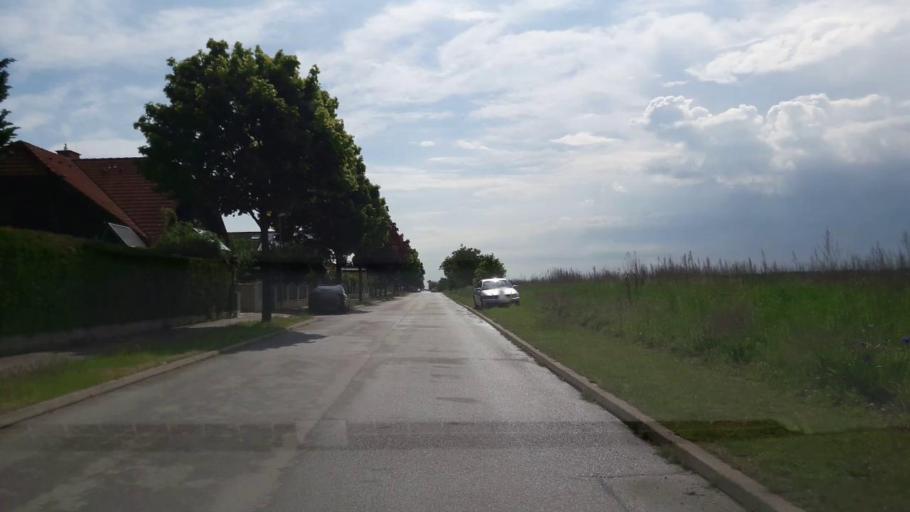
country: AT
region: Lower Austria
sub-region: Politischer Bezirk Ganserndorf
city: Deutsch-Wagram
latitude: 48.3148
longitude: 16.5874
